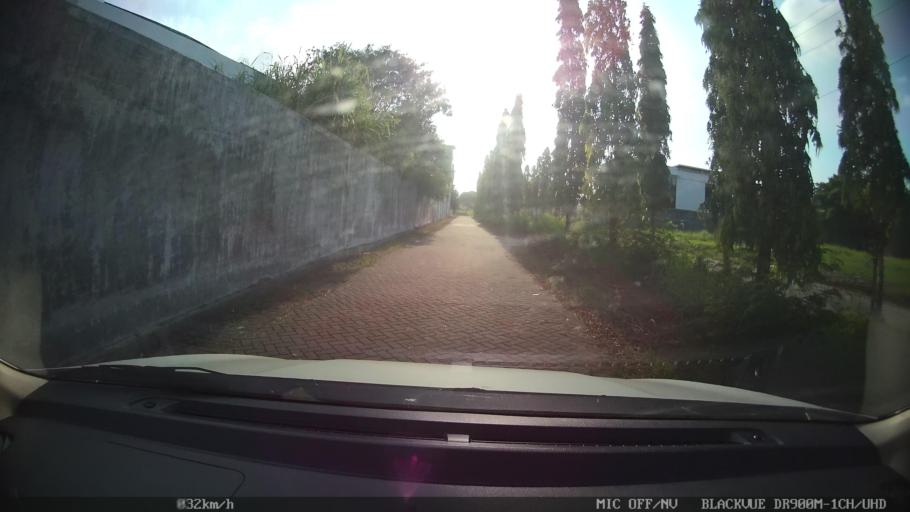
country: ID
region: North Sumatra
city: Medan
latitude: 3.6205
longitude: 98.6451
